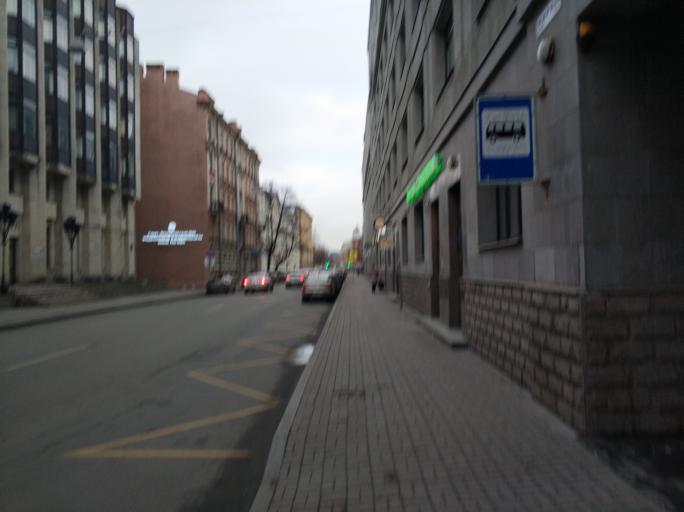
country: RU
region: St.-Petersburg
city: Petrogradka
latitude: 59.9602
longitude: 30.3181
